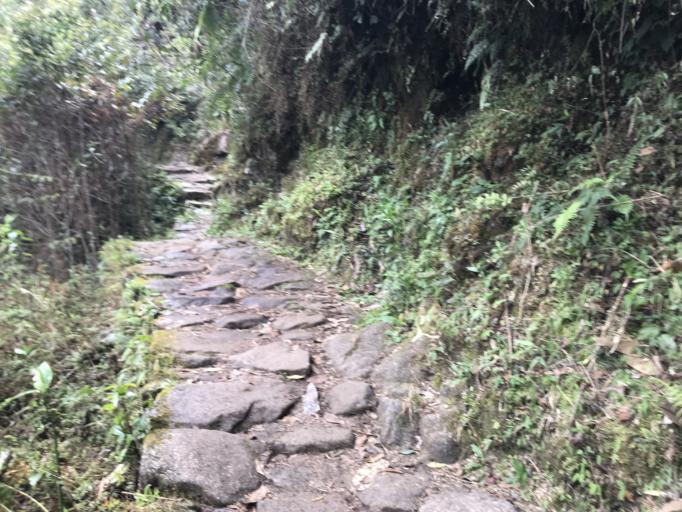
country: PE
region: Cusco
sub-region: Provincia de La Convencion
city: Santa Teresa
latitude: -13.1767
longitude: -72.5368
